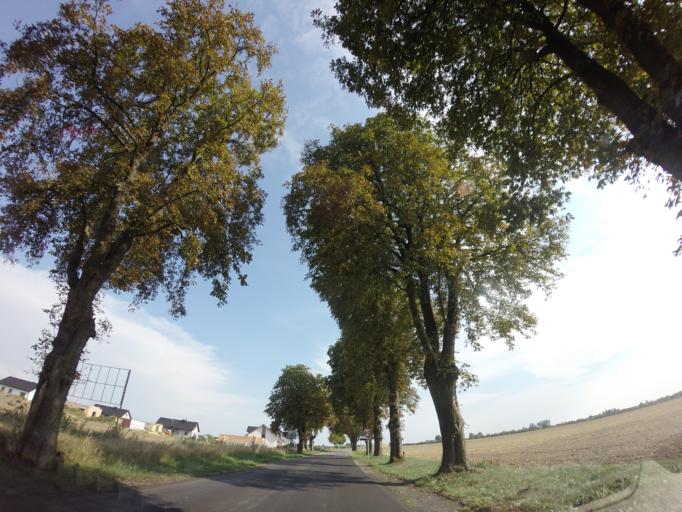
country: PL
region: West Pomeranian Voivodeship
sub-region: Powiat stargardzki
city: Stargard Szczecinski
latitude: 53.3106
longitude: 15.0448
